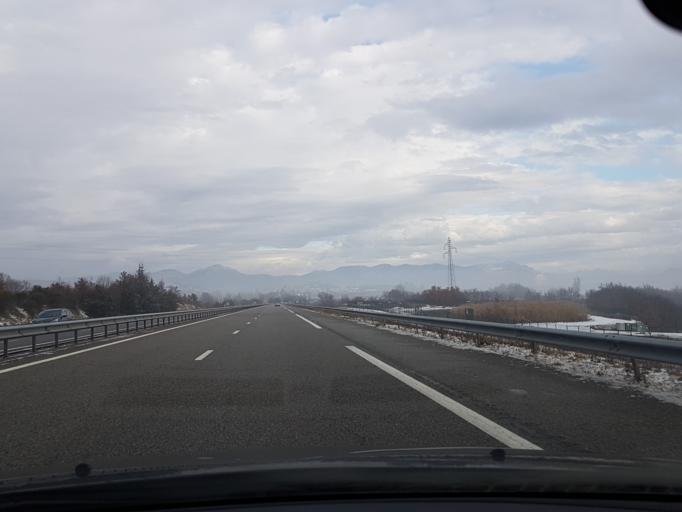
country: FR
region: Provence-Alpes-Cote d'Azur
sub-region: Departement des Hautes-Alpes
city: Laragne-Monteglin
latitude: 44.2761
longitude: 5.9000
